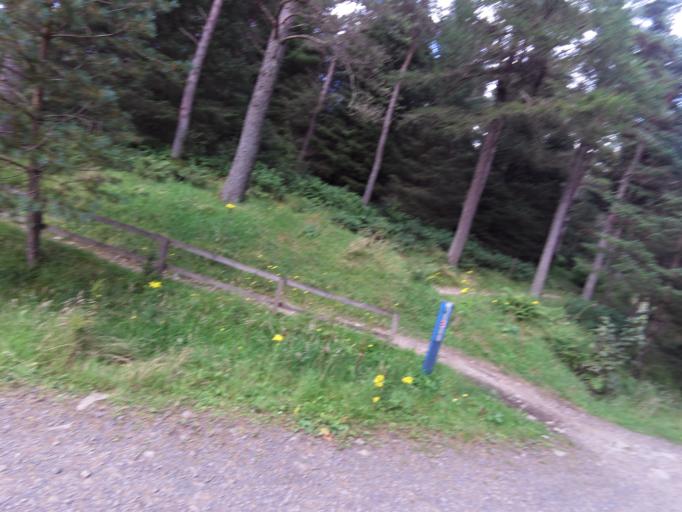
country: GB
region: Scotland
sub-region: The Scottish Borders
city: Peebles
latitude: 55.6631
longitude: -3.1332
